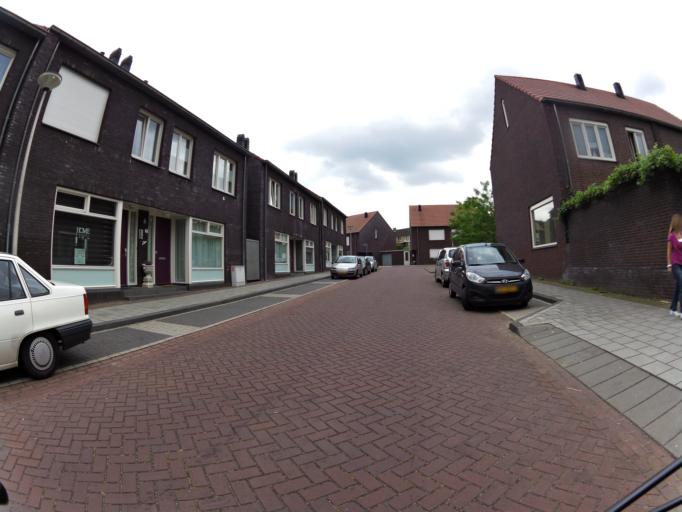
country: NL
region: Limburg
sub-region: Gemeente Heerlen
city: Heerlen
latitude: 50.9037
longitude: 6.0076
